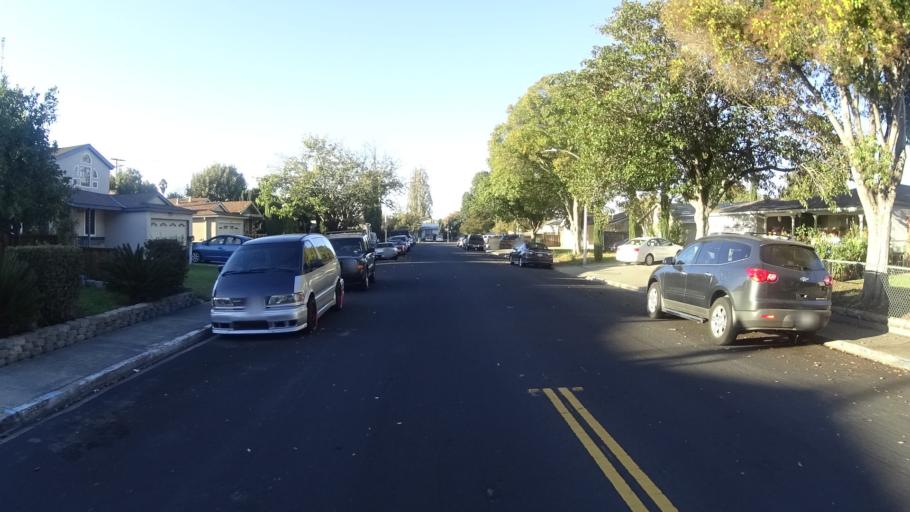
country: US
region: California
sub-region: Santa Clara County
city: Santa Clara
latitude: 37.3643
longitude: -121.9795
